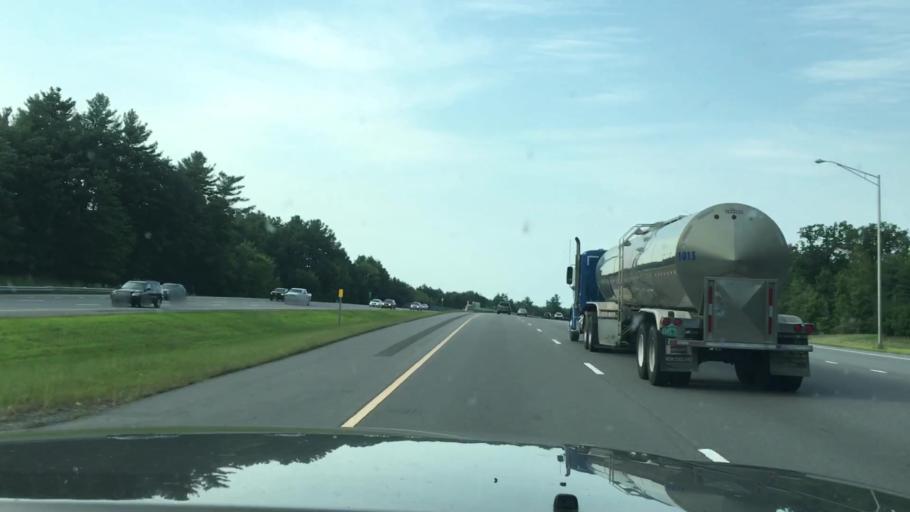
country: US
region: Massachusetts
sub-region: Middlesex County
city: Tyngsboro
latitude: 42.7014
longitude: -71.4495
